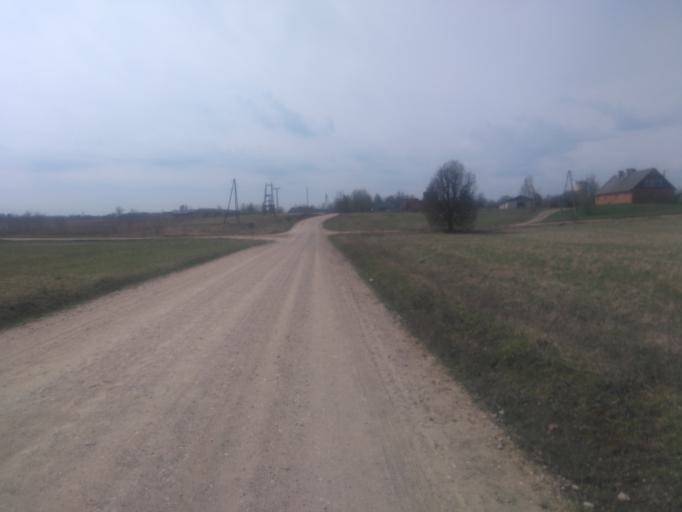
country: LV
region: Vecpiebalga
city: Vecpiebalga
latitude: 57.0222
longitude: 25.8389
